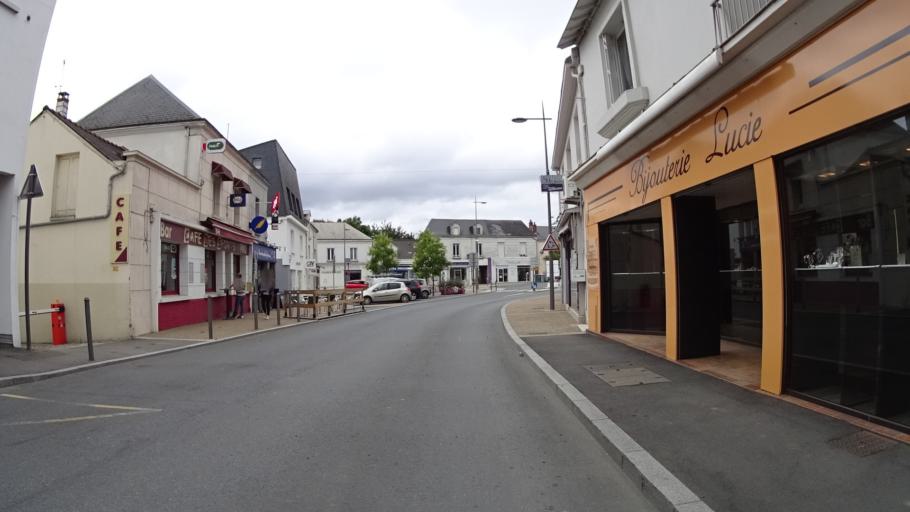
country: FR
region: Pays de la Loire
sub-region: Departement de la Loire-Atlantique
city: Thouare-sur-Loire
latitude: 47.2662
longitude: -1.4408
